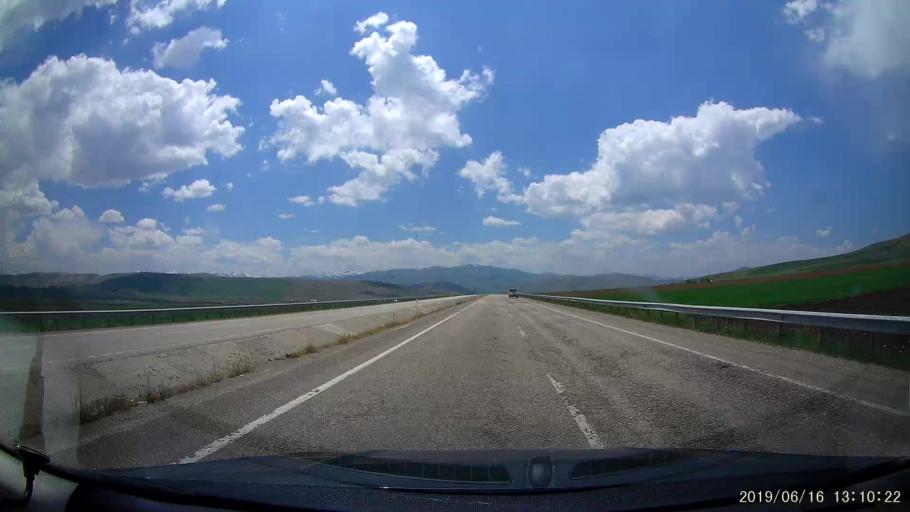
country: TR
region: Agri
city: Diyadin
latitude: 39.5955
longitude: 43.6340
